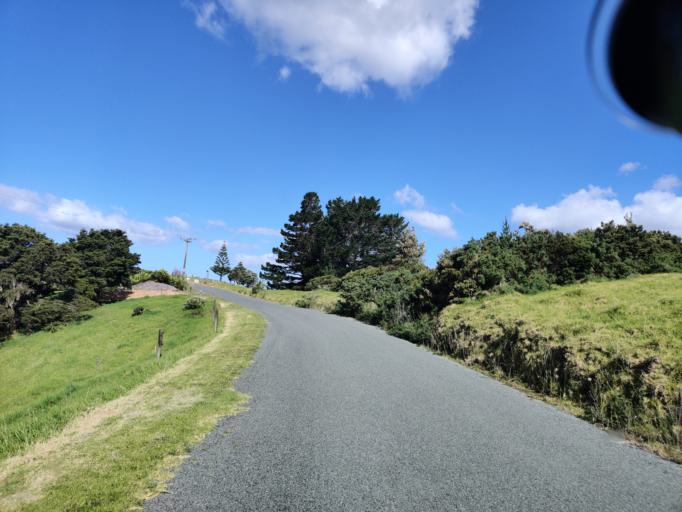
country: NZ
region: Northland
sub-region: Whangarei
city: Ngunguru
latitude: -35.6075
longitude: 174.5272
